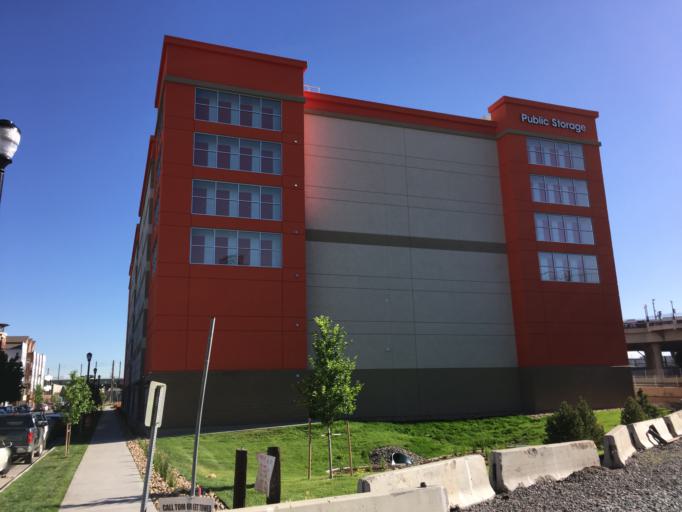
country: US
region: Colorado
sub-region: Denver County
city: Denver
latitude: 39.7585
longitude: -104.9952
